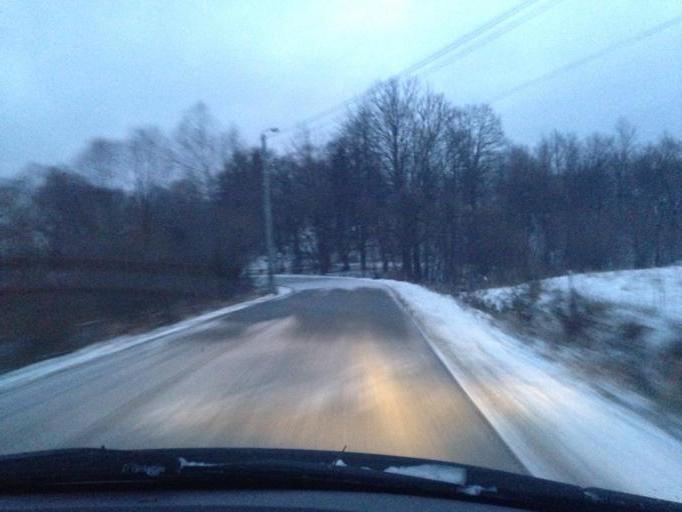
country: PL
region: Subcarpathian Voivodeship
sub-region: Powiat jasielski
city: Krempna
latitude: 49.5261
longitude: 21.5539
